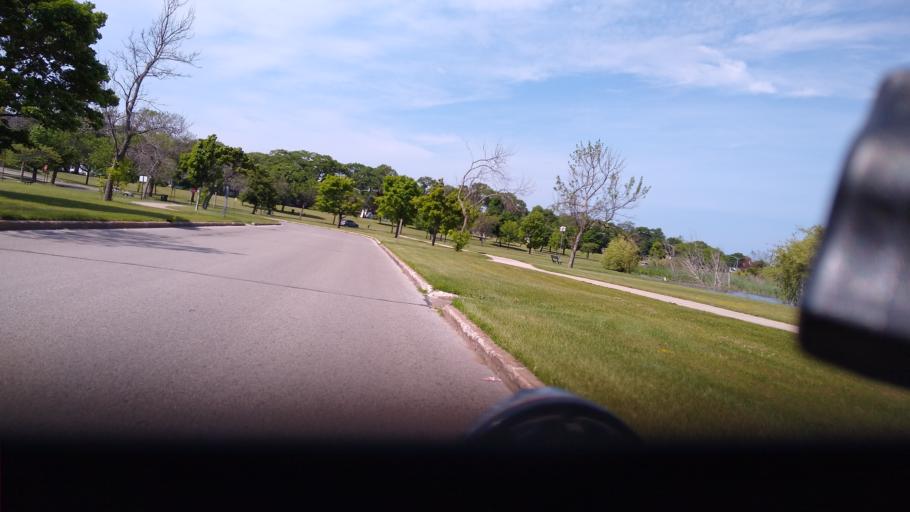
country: US
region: Michigan
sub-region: Delta County
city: Escanaba
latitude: 45.7406
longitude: -87.0496
